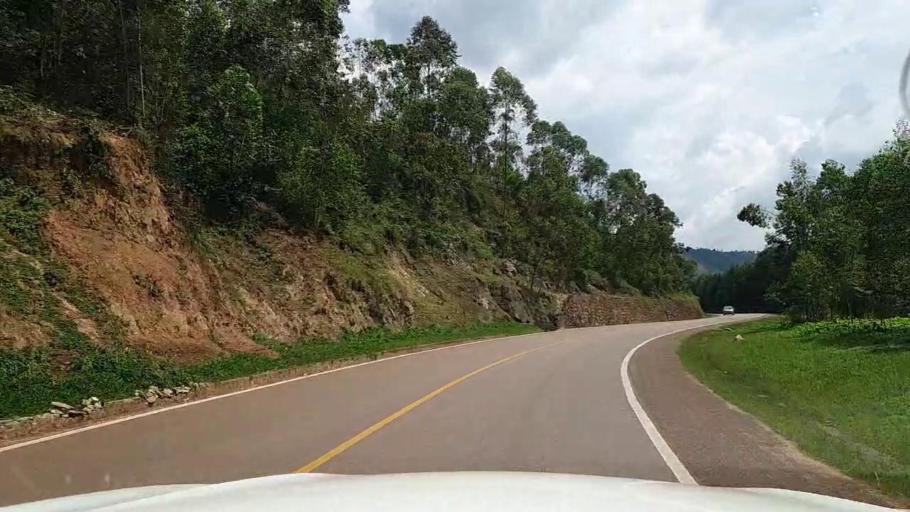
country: RW
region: Kigali
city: Kigali
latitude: -1.8181
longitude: 30.0895
